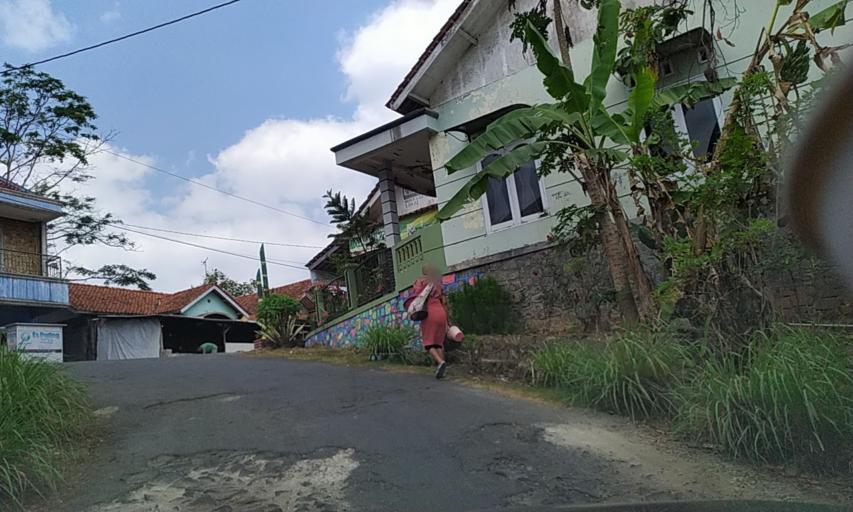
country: ID
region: Central Java
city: Kubang
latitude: -7.2658
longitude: 108.6514
